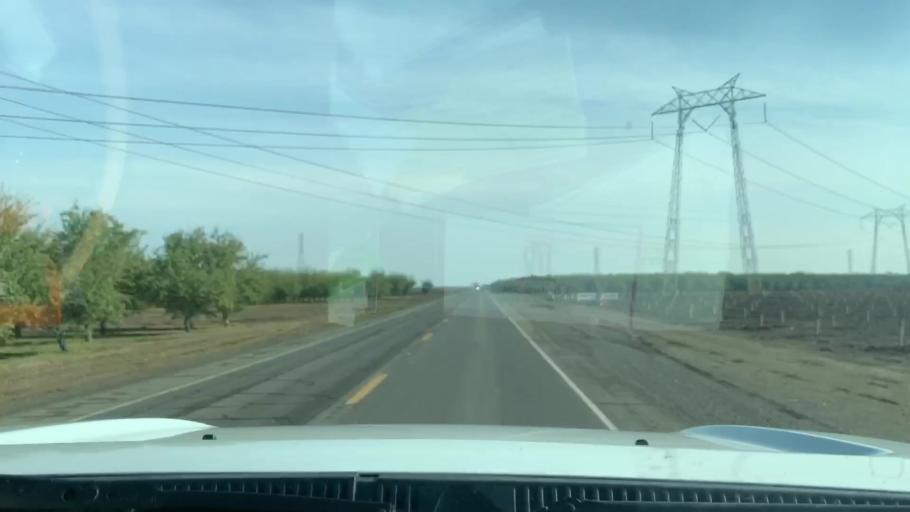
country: US
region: California
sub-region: Fresno County
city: Huron
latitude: 36.2547
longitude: -120.2225
